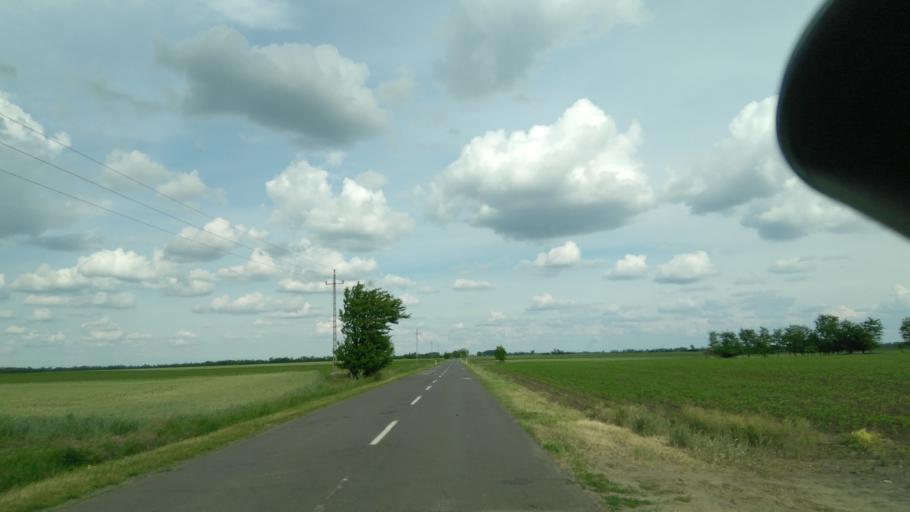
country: RO
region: Arad
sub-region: Comuna Peregu Mare
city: Peregu Mic
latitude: 46.2990
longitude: 20.9418
